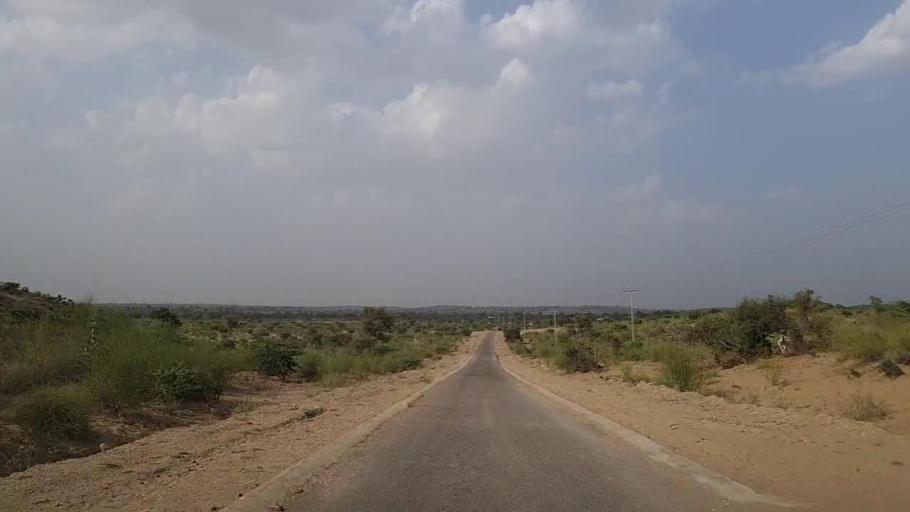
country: PK
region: Sindh
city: Islamkot
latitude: 24.7904
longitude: 70.2012
